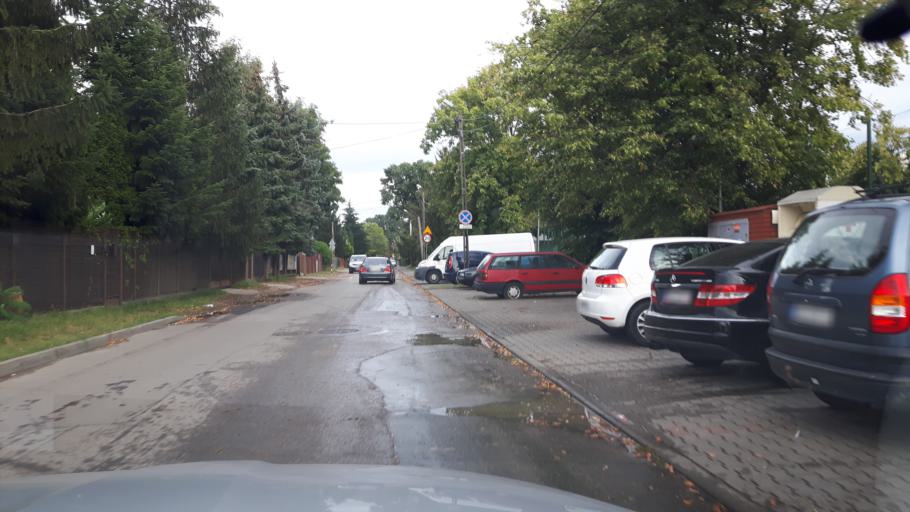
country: PL
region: Masovian Voivodeship
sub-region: Powiat wolominski
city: Marki
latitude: 52.3248
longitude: 21.0990
